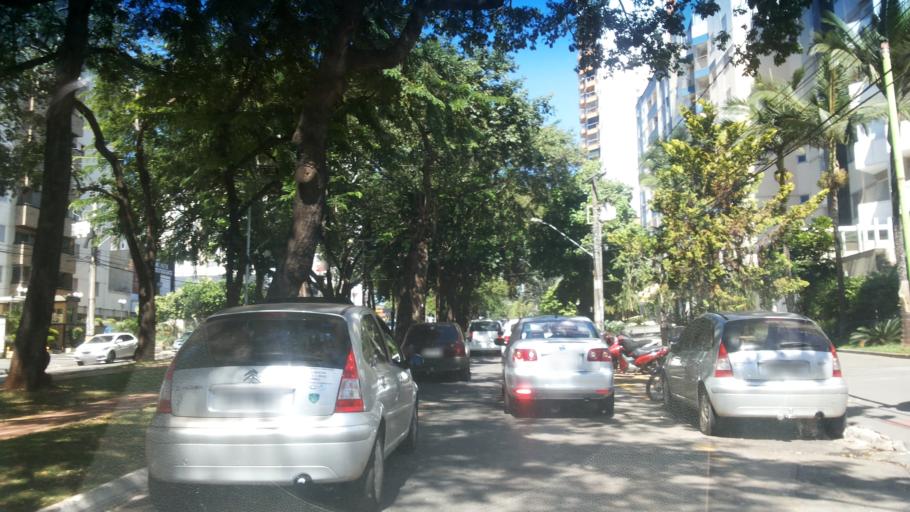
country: BR
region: Goias
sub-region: Goiania
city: Goiania
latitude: -16.7106
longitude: -49.2589
